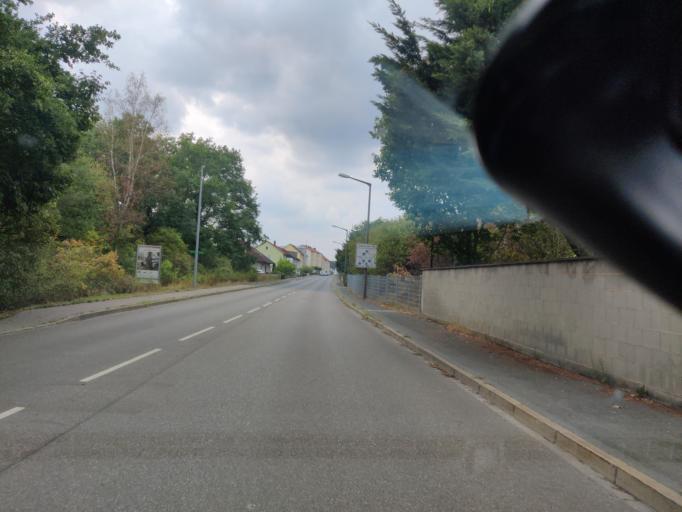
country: DE
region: Bavaria
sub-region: Regierungsbezirk Mittelfranken
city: Roth
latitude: 49.2480
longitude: 11.1018
